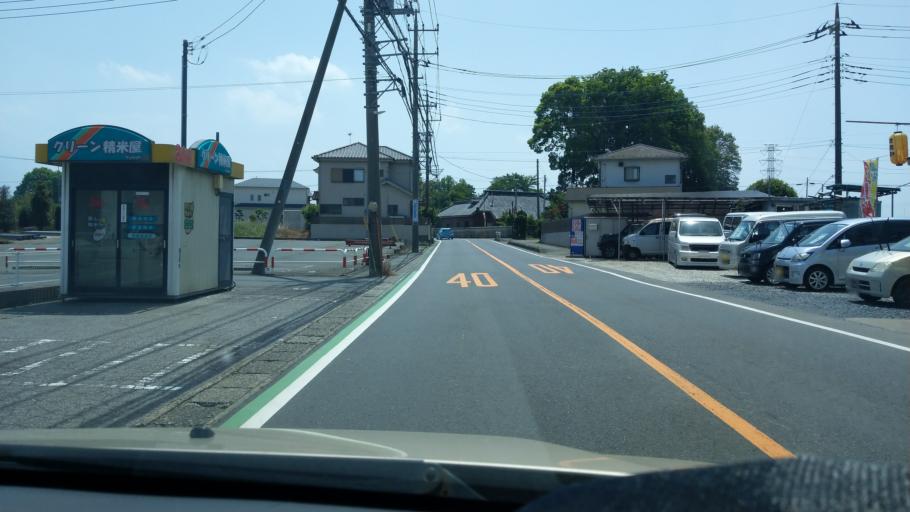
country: JP
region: Saitama
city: Iwatsuki
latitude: 35.9166
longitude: 139.7218
